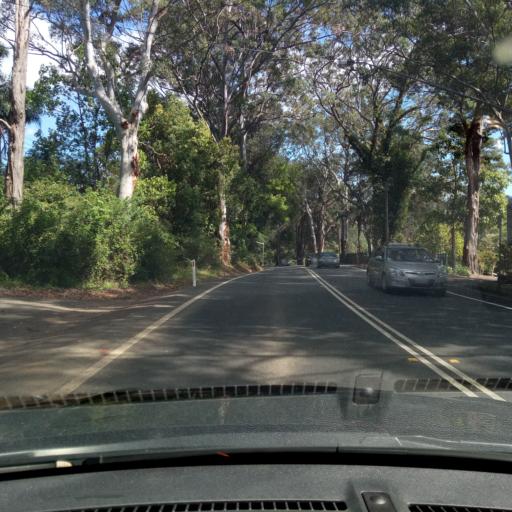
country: AU
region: New South Wales
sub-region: Gosford Shire
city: Lisarow
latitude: -33.3843
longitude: 151.3587
